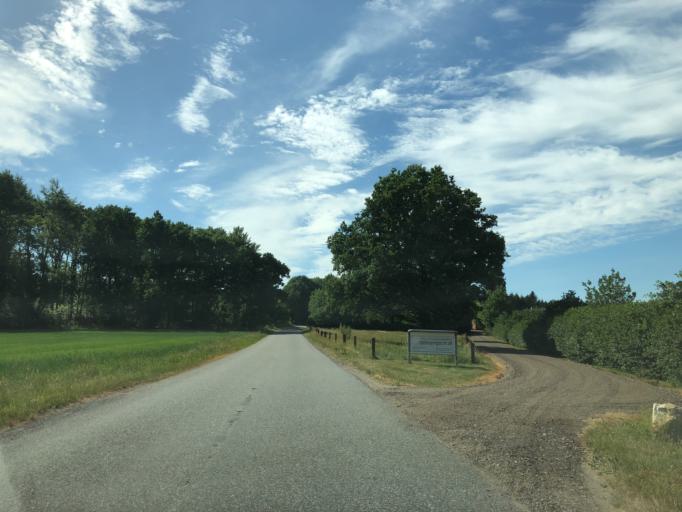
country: DK
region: Central Jutland
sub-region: Herning Kommune
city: Lind
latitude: 56.0182
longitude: 8.9760
